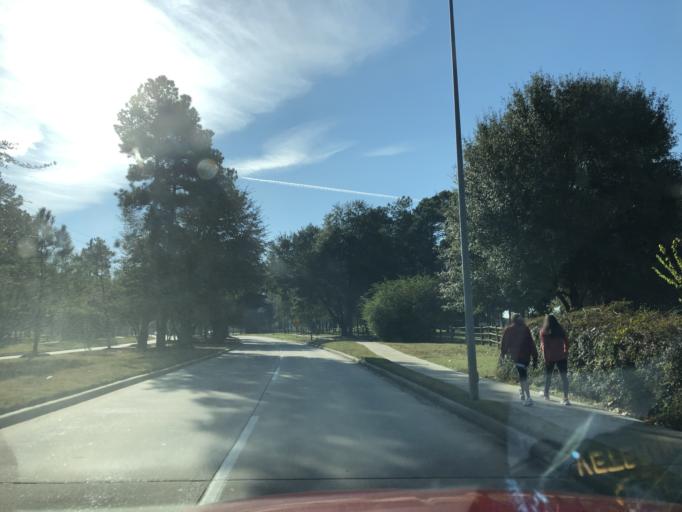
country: US
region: Texas
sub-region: Harris County
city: Tomball
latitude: 30.0392
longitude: -95.5627
